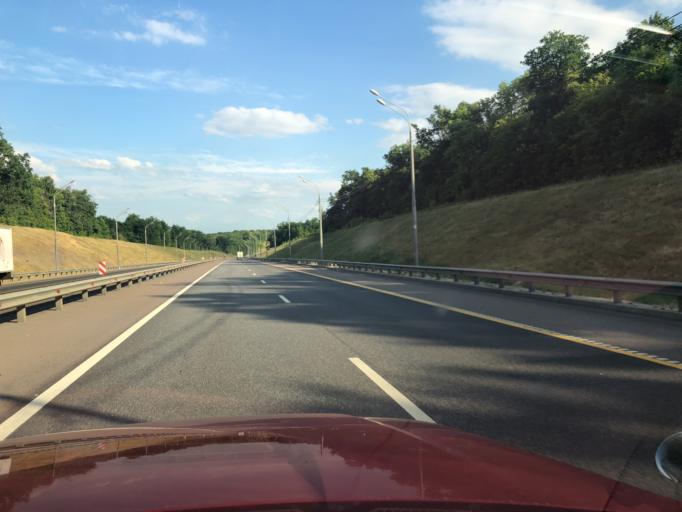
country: RU
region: Lipetsk
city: Zadonsk
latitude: 52.4111
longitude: 38.8485
